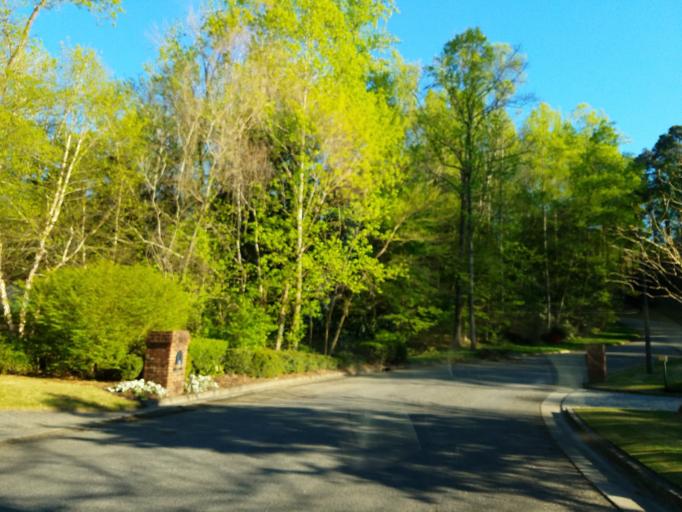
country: US
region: Georgia
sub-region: Cobb County
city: Vinings
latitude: 33.8515
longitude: -84.4539
